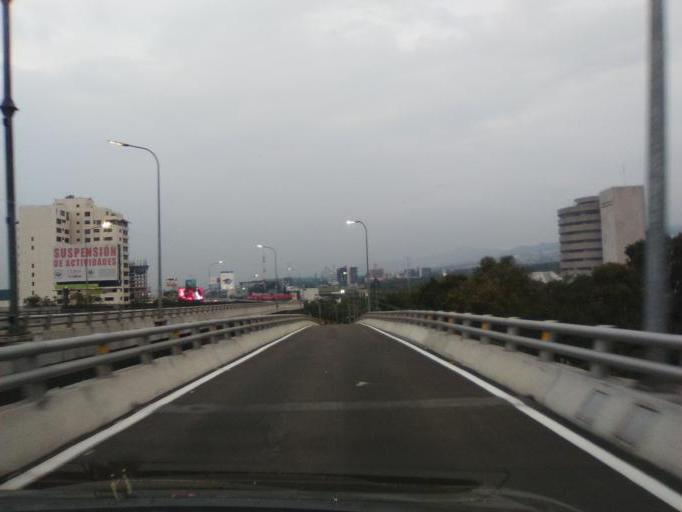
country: MX
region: Mexico City
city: Magdalena Contreras
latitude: 19.3107
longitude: -99.2191
